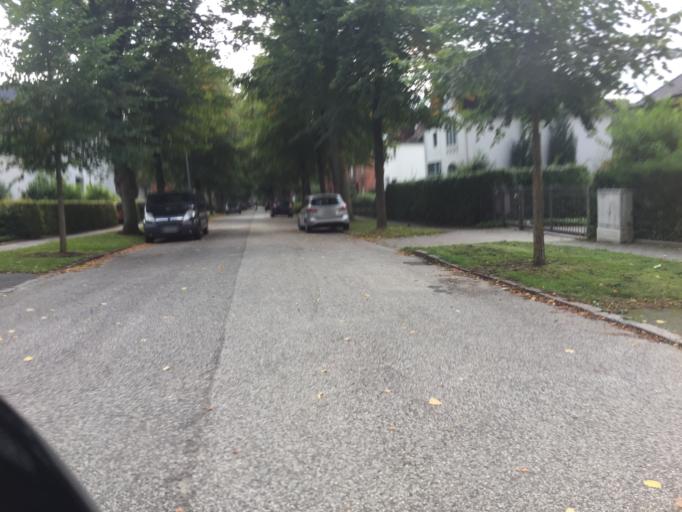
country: DE
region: Schleswig-Holstein
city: Itzehoe
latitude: 53.9355
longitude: 9.5116
